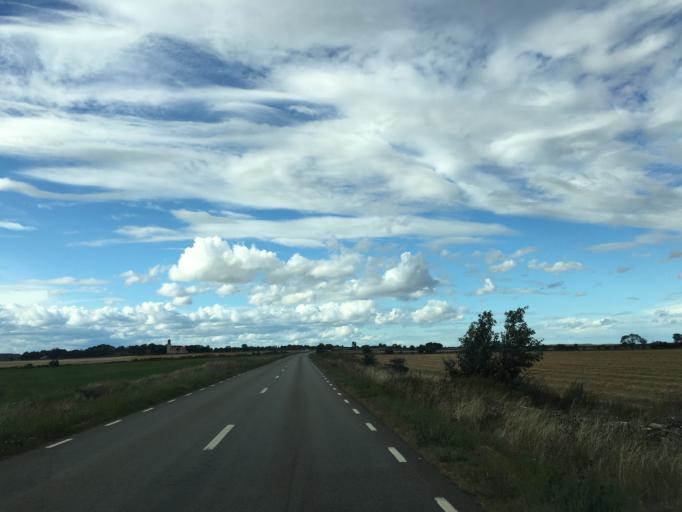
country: SE
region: Kalmar
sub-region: Morbylanga Kommun
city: Moerbylanga
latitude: 56.3970
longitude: 16.4365
